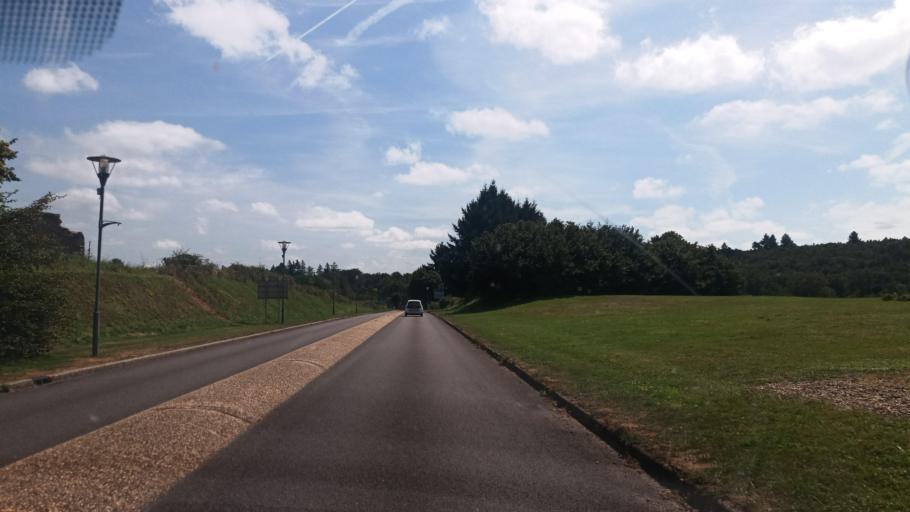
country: FR
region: Limousin
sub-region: Departement de la Haute-Vienne
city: Oradour-sur-Glane
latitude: 45.9292
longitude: 1.0359
